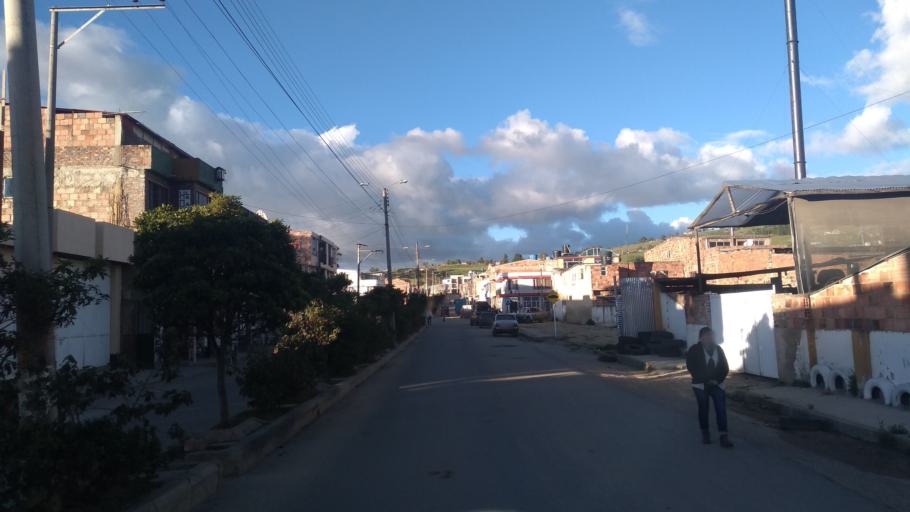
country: CO
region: Boyaca
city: Toca
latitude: 5.5660
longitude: -73.1861
